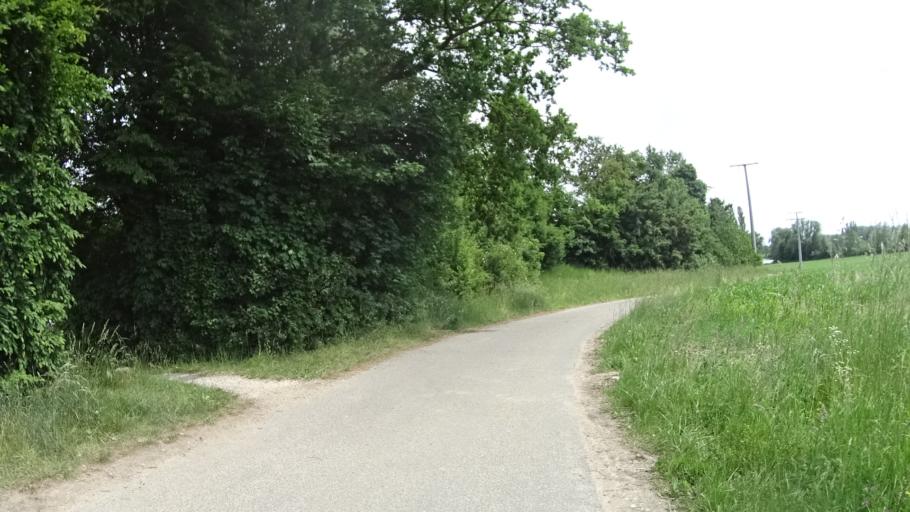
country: DE
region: Bavaria
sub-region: Upper Palatinate
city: Donaustauf
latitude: 49.0284
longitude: 12.2335
